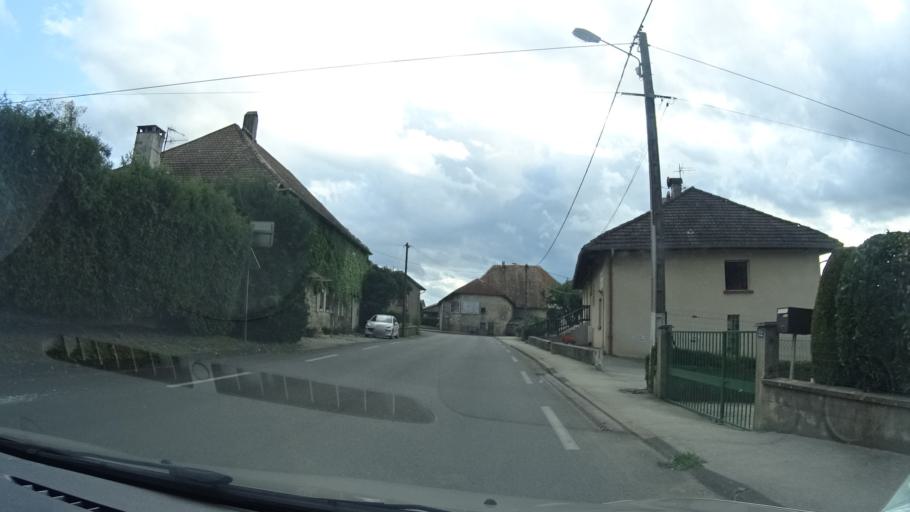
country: FR
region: Franche-Comte
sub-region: Departement du Doubs
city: Saone
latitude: 47.2213
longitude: 6.1136
